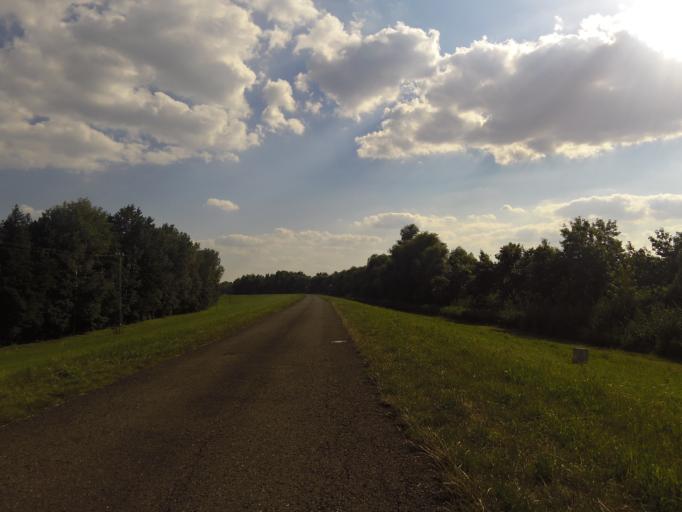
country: HU
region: Jasz-Nagykun-Szolnok
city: Abadszalok
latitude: 47.5170
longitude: 20.5889
